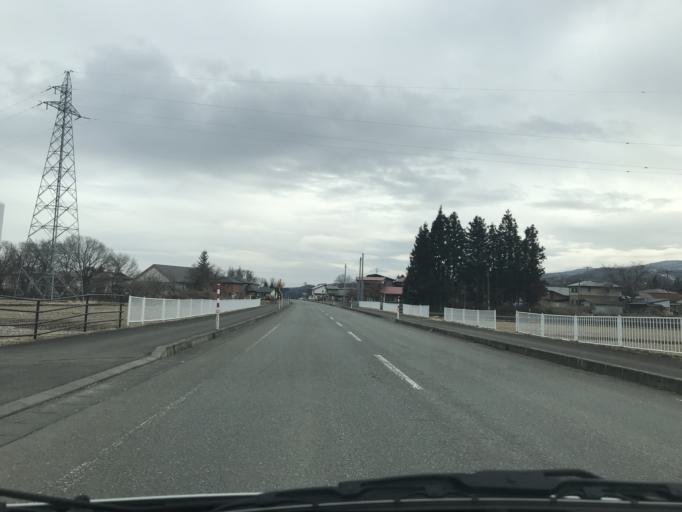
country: JP
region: Iwate
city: Kitakami
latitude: 39.3144
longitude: 140.9754
